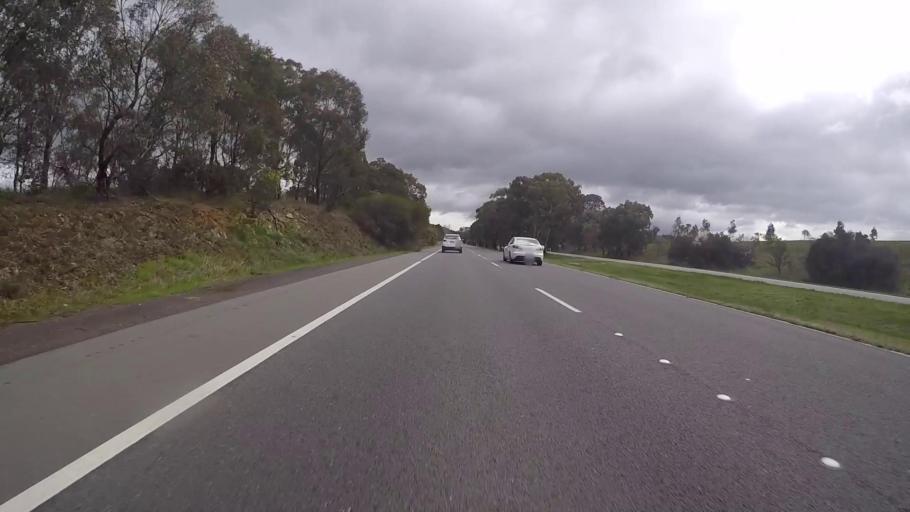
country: AU
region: Australian Capital Territory
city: Kaleen
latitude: -35.2080
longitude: 149.1053
